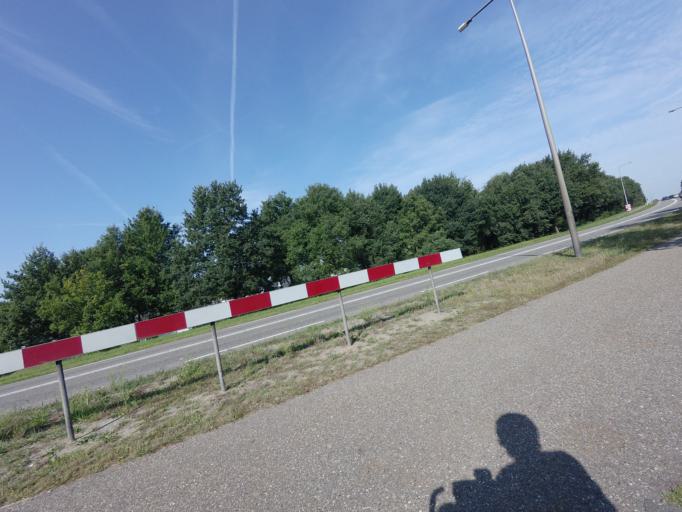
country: NL
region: Overijssel
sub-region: Gemeente Hardenberg
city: Hardenberg
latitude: 52.5739
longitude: 6.6361
